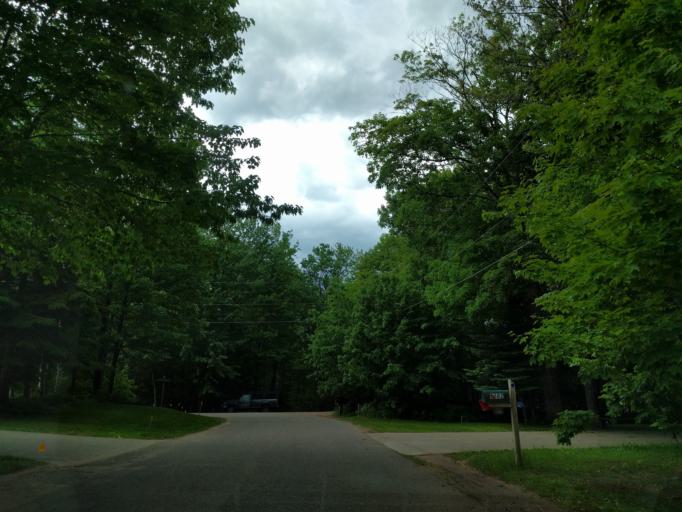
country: US
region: Michigan
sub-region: Marquette County
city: Trowbridge Park
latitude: 46.5634
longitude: -87.4444
